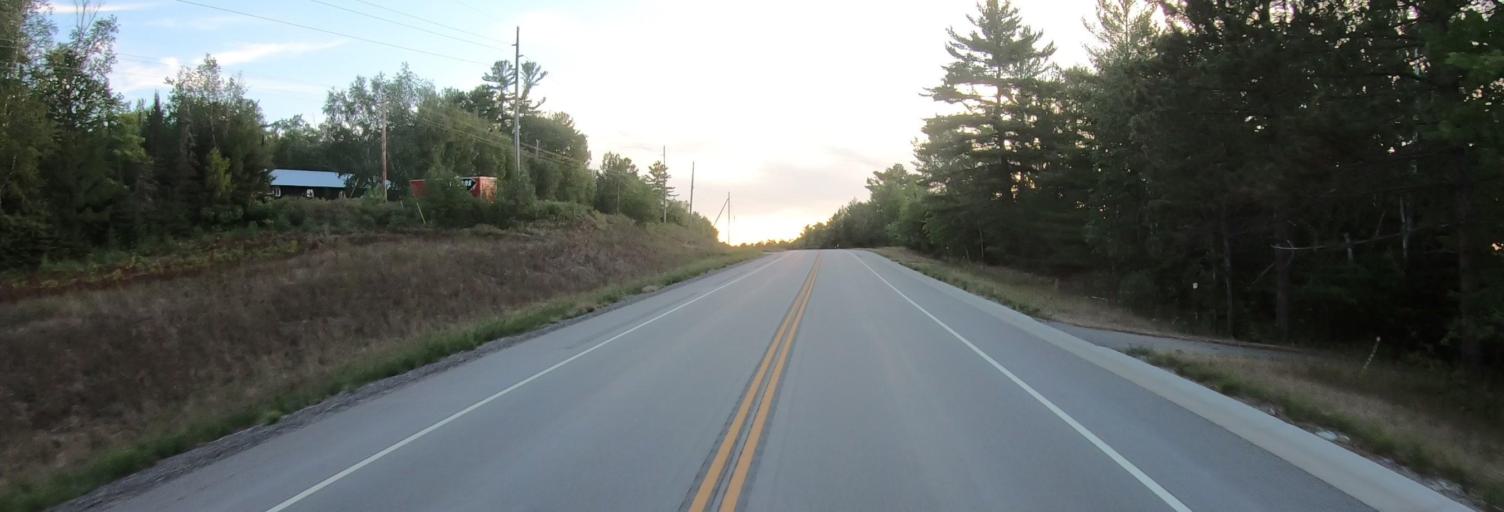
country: US
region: Minnesota
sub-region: Saint Louis County
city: Babbitt
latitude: 47.8571
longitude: -92.0688
